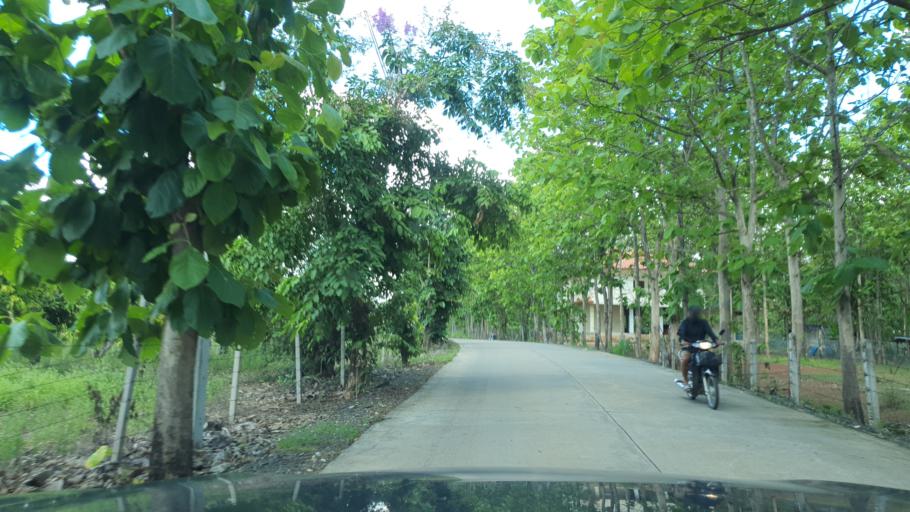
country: TH
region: Chiang Mai
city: San Sai
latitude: 18.9221
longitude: 99.0436
